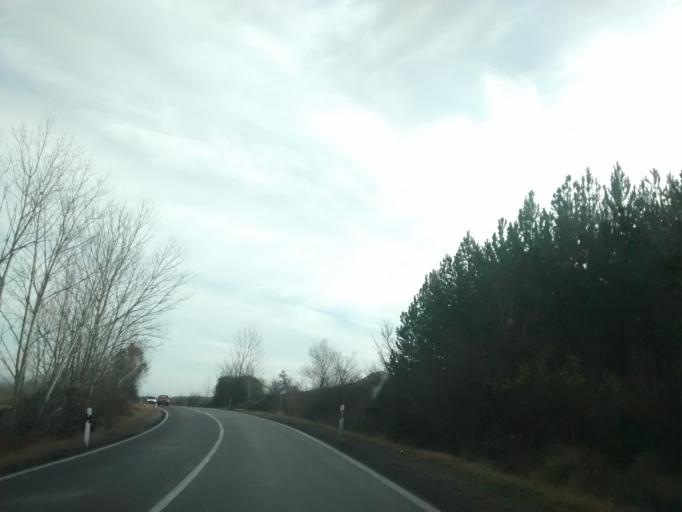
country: ES
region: Aragon
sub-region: Provincia de Huesca
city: Bailo
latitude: 42.5543
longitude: -0.7683
